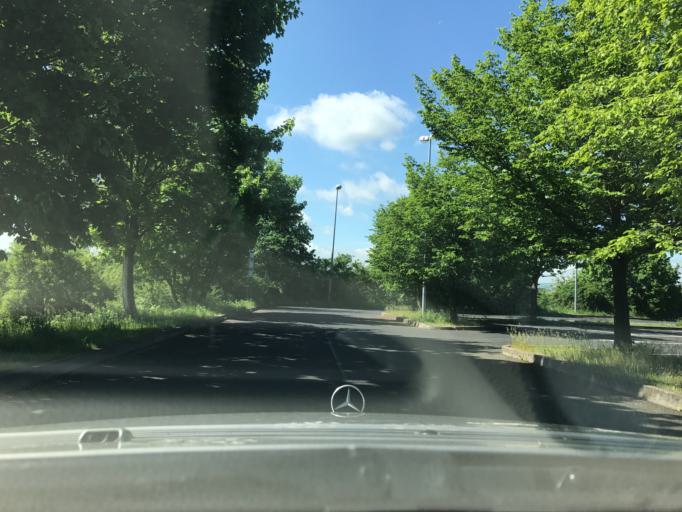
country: DE
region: Thuringia
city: Muehlhausen
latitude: 51.1956
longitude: 10.4846
